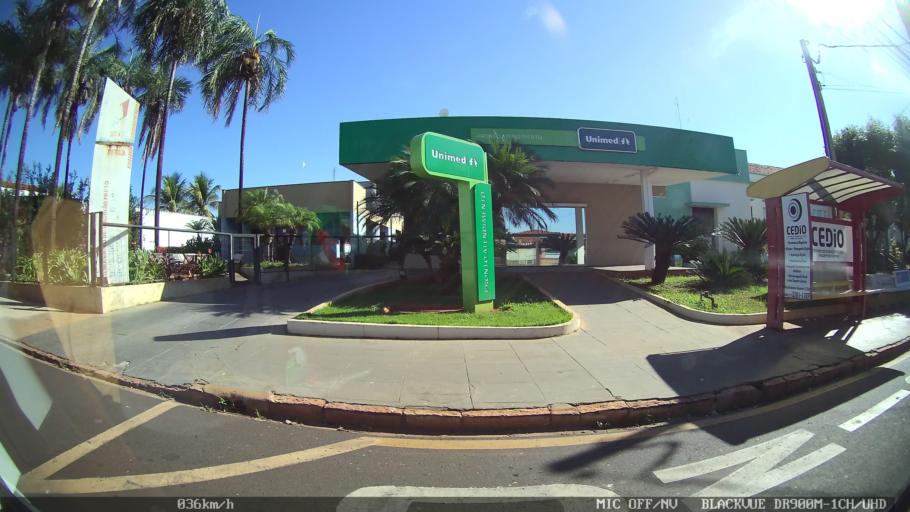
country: BR
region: Sao Paulo
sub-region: Olimpia
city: Olimpia
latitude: -20.7360
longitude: -48.9180
